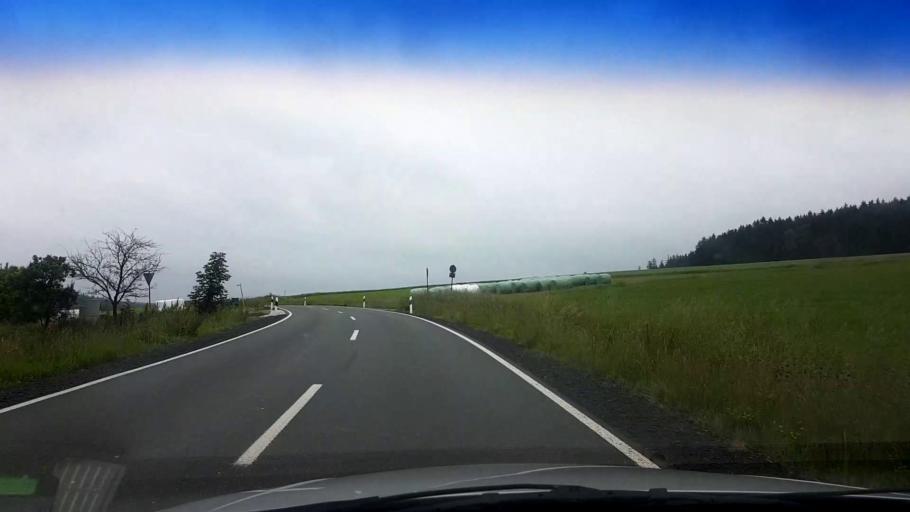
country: DE
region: Bavaria
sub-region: Upper Franconia
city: Arzberg
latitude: 50.0310
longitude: 12.1841
